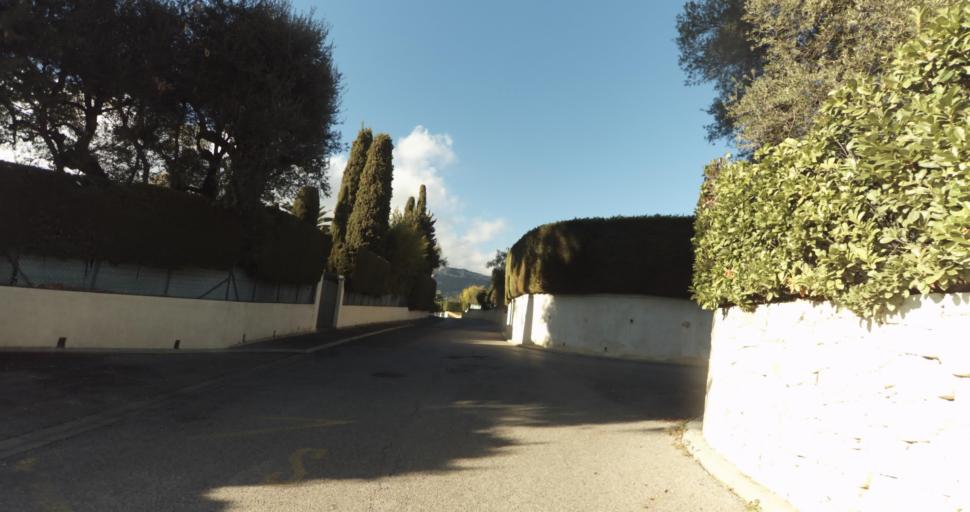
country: FR
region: Provence-Alpes-Cote d'Azur
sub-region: Departement des Alpes-Maritimes
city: La Gaude
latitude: 43.7123
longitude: 7.1357
